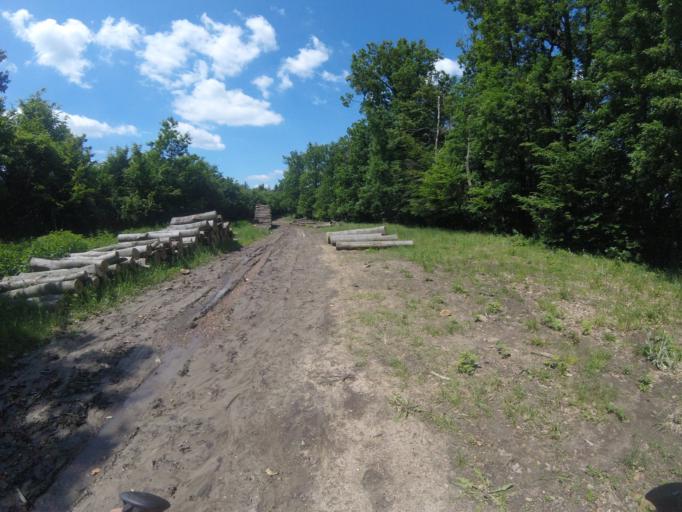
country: HU
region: Nograd
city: Batonyterenye
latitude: 47.9323
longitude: 19.8108
